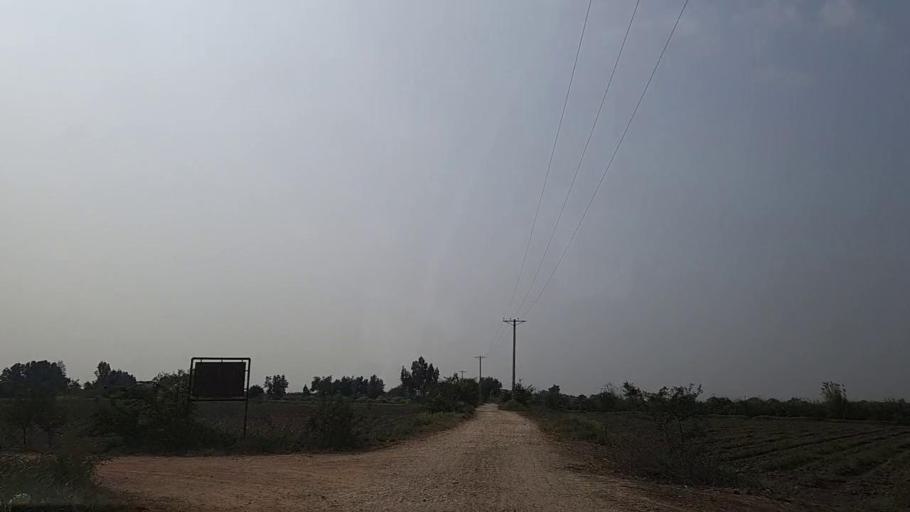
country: PK
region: Sindh
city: Mirpur Sakro
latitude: 24.6181
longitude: 67.7420
